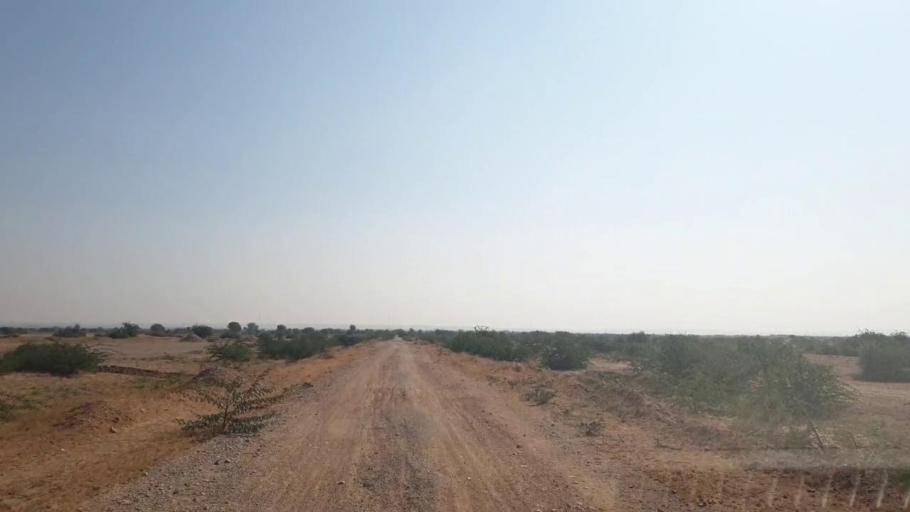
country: PK
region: Sindh
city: Gharo
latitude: 25.1416
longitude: 67.7311
